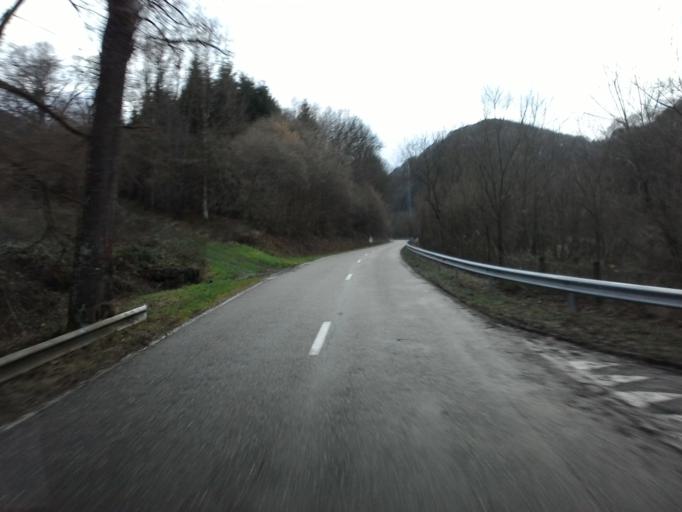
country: BE
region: Wallonia
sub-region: Province de Liege
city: Aywaille
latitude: 50.4425
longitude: 5.7377
